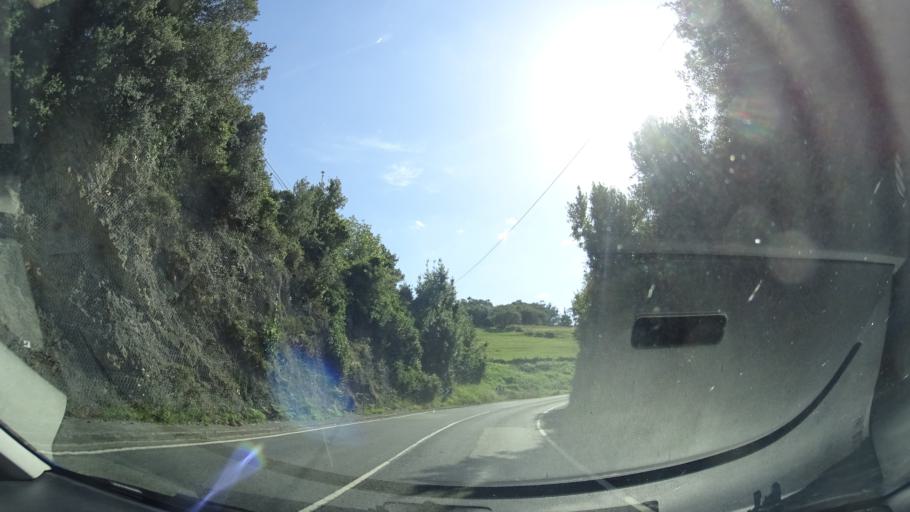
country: ES
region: Basque Country
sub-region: Bizkaia
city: Bakio
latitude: 43.4343
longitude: -2.7931
